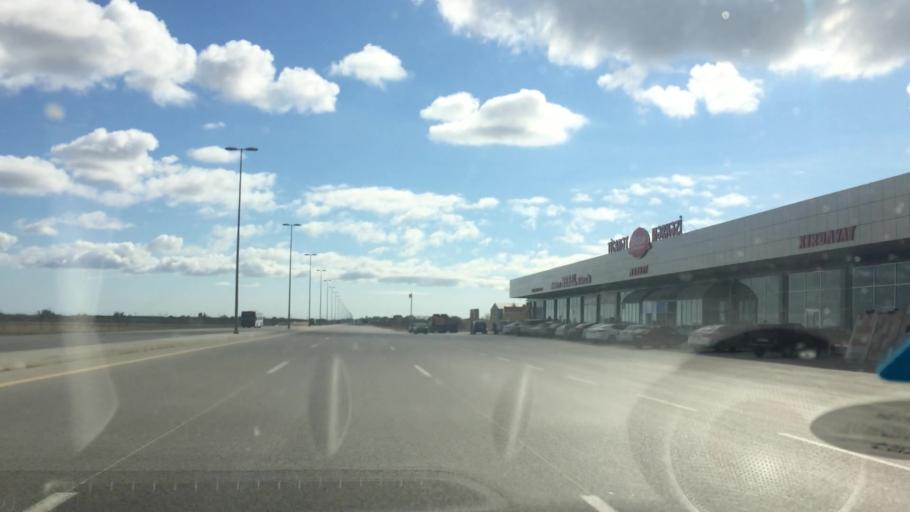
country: AZ
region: Baki
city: Qala
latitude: 40.4562
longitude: 50.1424
